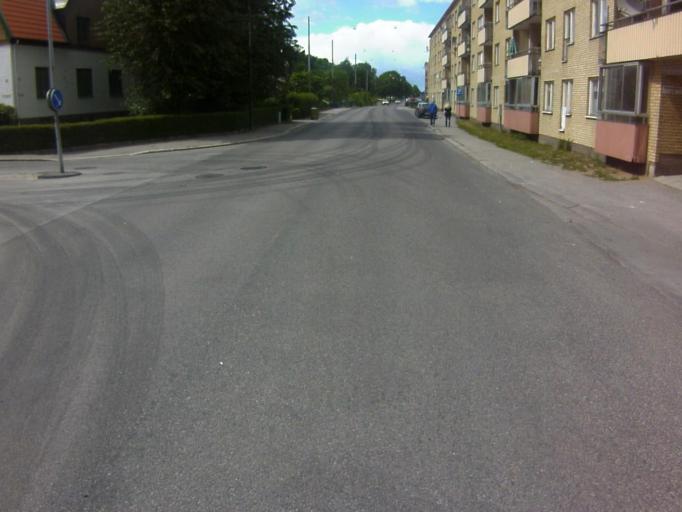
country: SE
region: Soedermanland
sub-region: Eskilstuna Kommun
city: Eskilstuna
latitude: 59.3672
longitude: 16.5047
